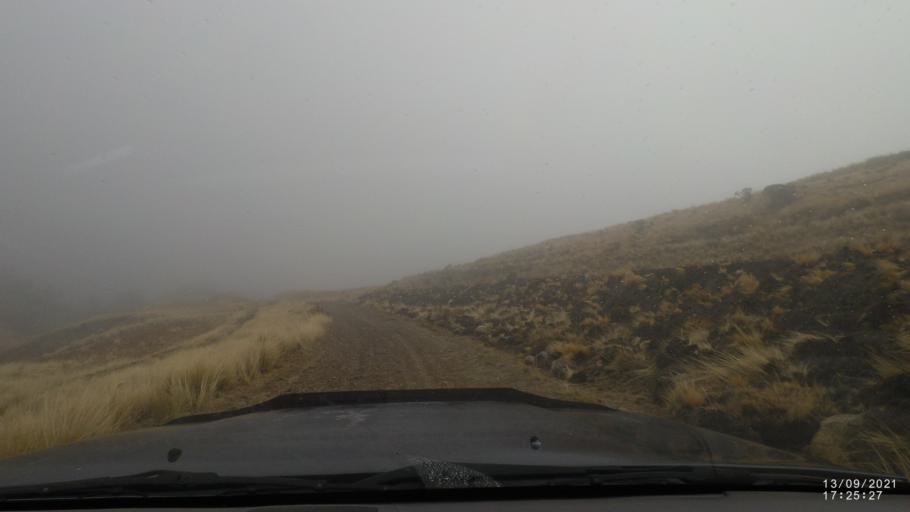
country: BO
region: Cochabamba
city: Colomi
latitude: -17.3584
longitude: -65.7812
